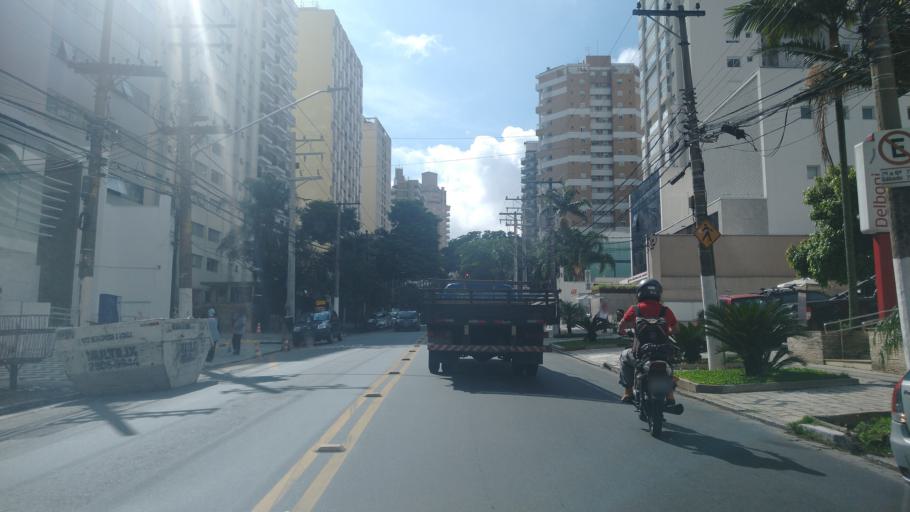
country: BR
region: Sao Paulo
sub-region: Sao Paulo
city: Sao Paulo
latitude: -23.4857
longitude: -46.6290
